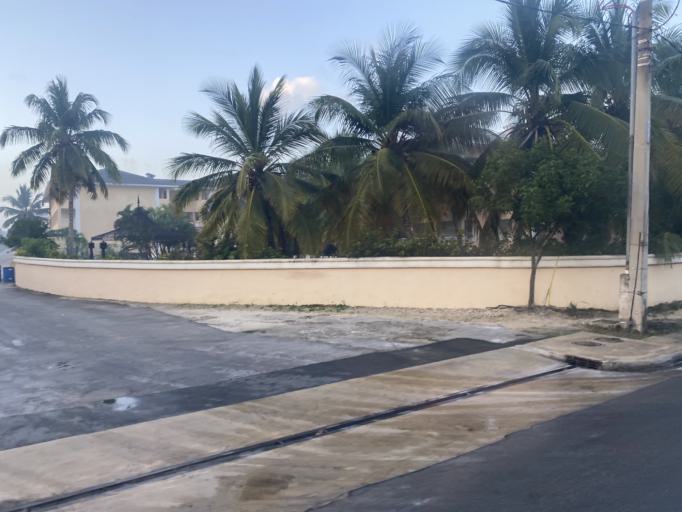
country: DO
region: San Juan
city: Punta Cana
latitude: 18.7191
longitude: -68.4735
